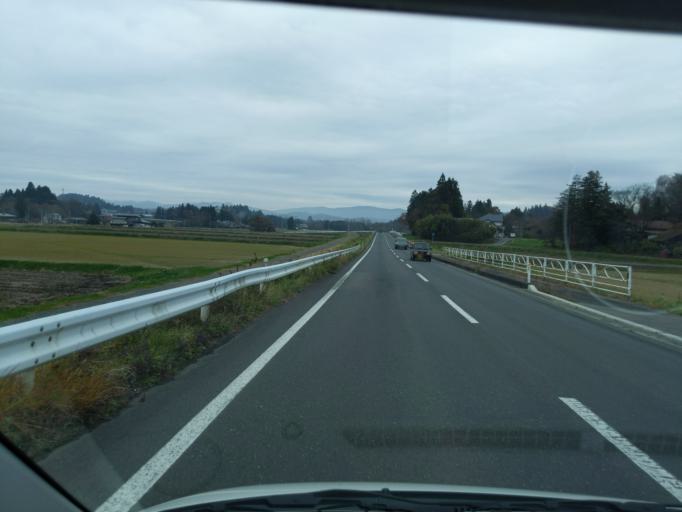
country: JP
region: Iwate
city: Mizusawa
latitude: 39.2130
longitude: 141.2214
